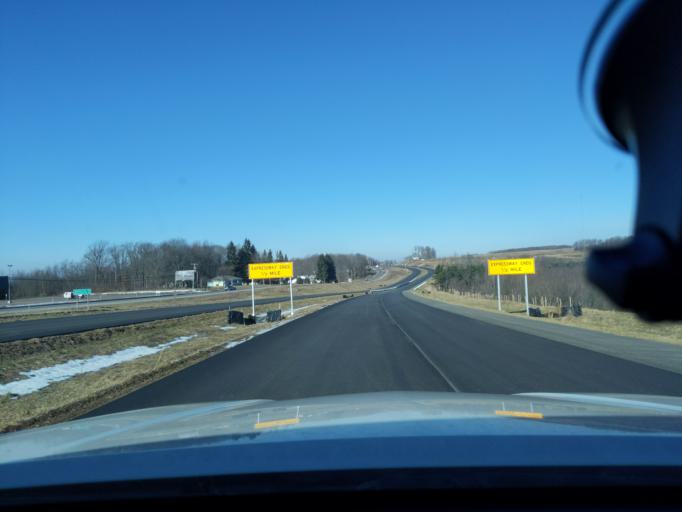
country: US
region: Pennsylvania
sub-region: Somerset County
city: Meyersdale
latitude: 39.6957
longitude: -79.0985
